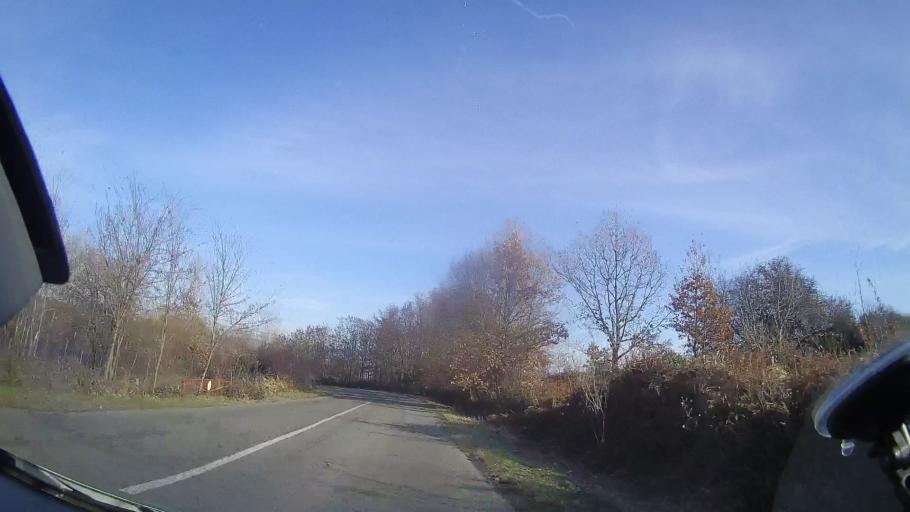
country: RO
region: Bihor
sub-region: Comuna Brusturi
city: Brusturi
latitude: 47.1099
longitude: 22.2594
